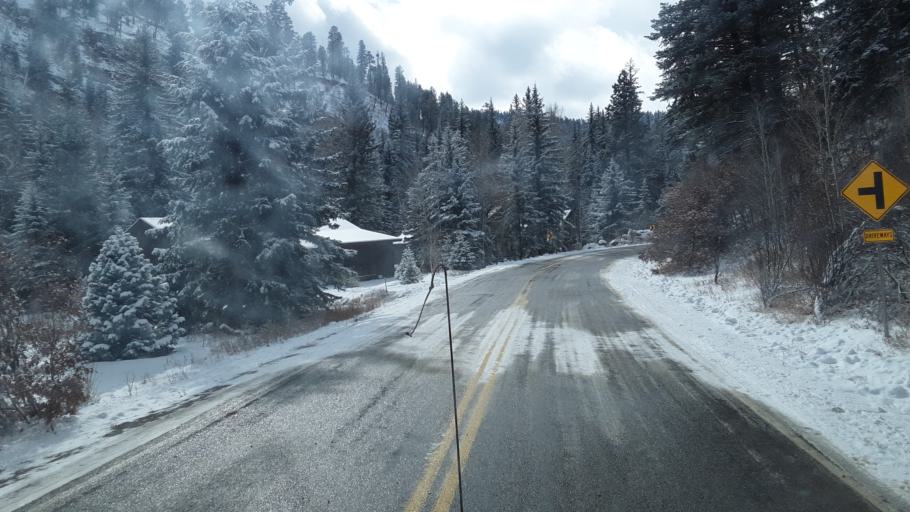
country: US
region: Colorado
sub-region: La Plata County
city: Bayfield
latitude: 37.3650
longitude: -107.6674
